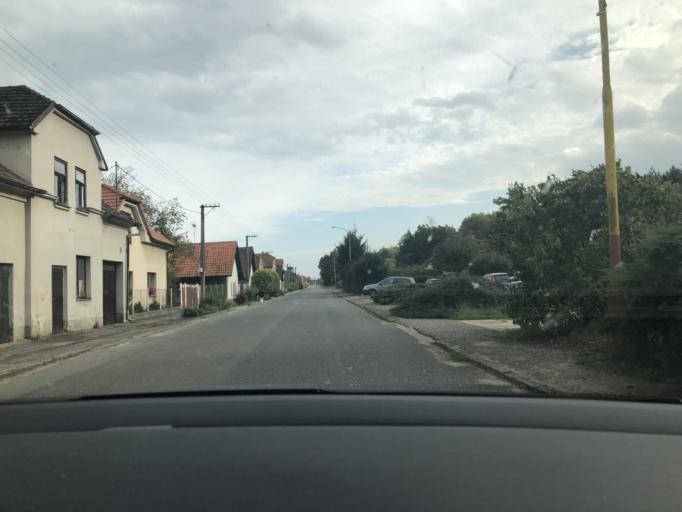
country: CZ
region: Central Bohemia
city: Zizelice
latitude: 50.0965
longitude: 15.4372
